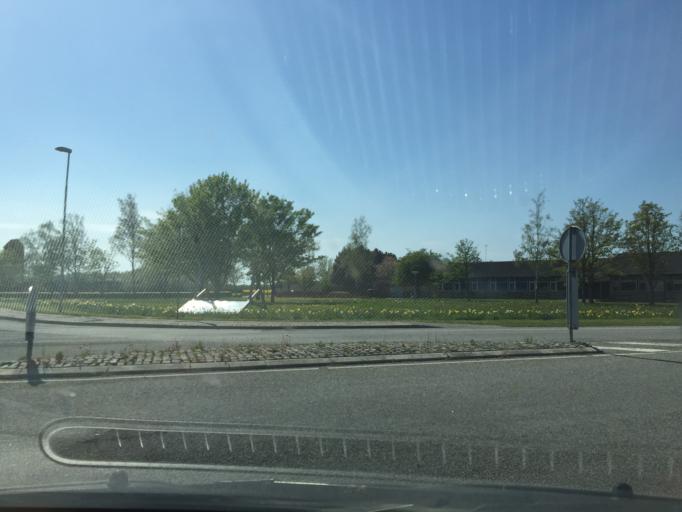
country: DK
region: Zealand
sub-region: Lolland Kommune
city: Rodbyhavn
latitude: 54.6676
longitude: 11.3639
